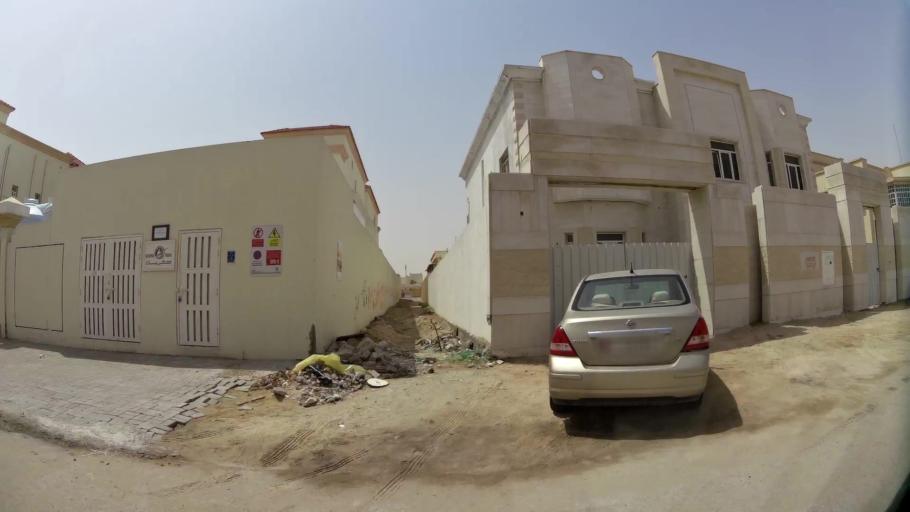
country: QA
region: Baladiyat ar Rayyan
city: Ar Rayyan
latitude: 25.2307
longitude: 51.4165
